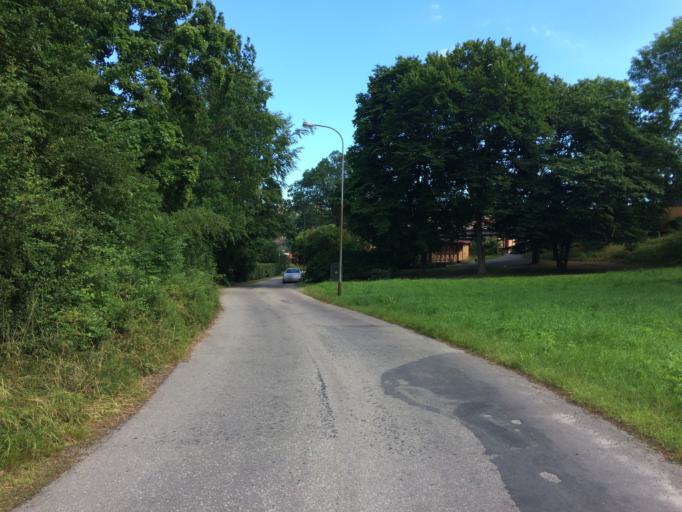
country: SE
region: Stockholm
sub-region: Nacka Kommun
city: Nacka
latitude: 59.3223
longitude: 18.1535
